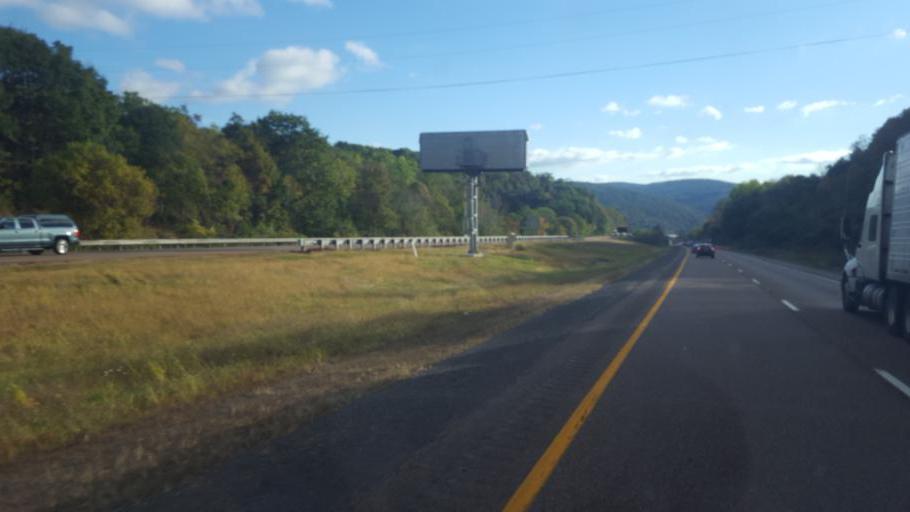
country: US
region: Maryland
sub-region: Allegany County
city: Frostburg
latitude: 39.6344
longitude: -78.9068
